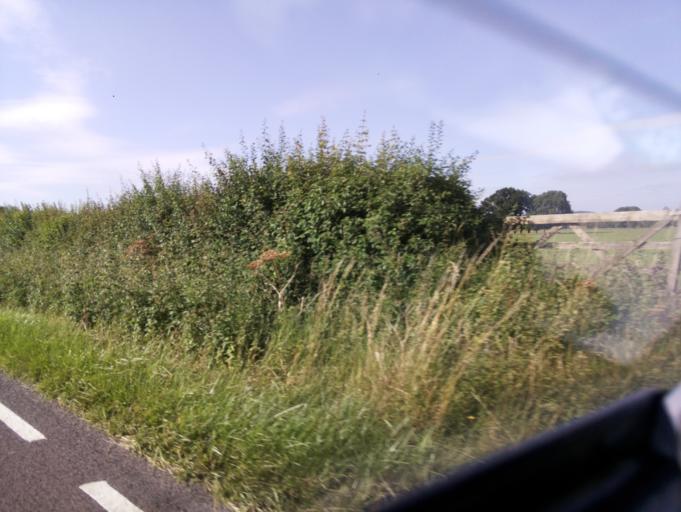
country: GB
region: England
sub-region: Oxfordshire
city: Faringdon
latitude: 51.6719
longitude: -1.5872
